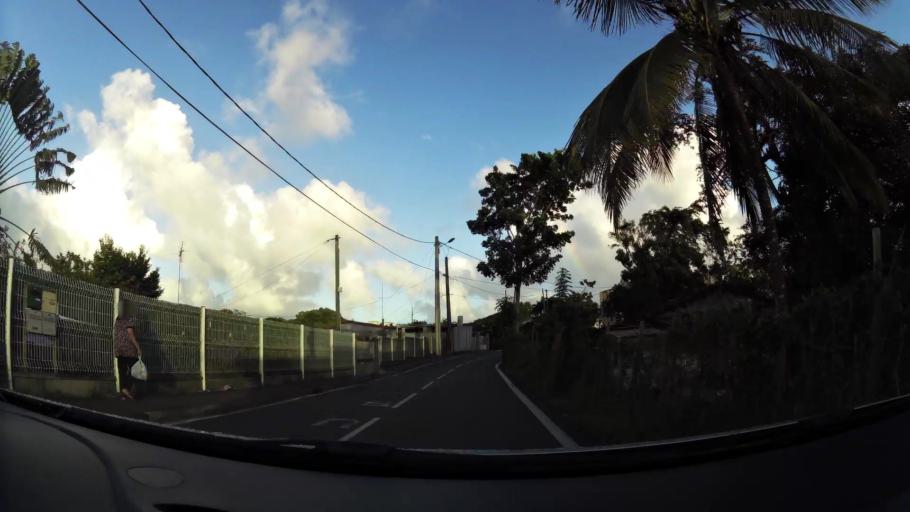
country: MQ
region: Martinique
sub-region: Martinique
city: Fort-de-France
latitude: 14.6360
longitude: -61.0704
